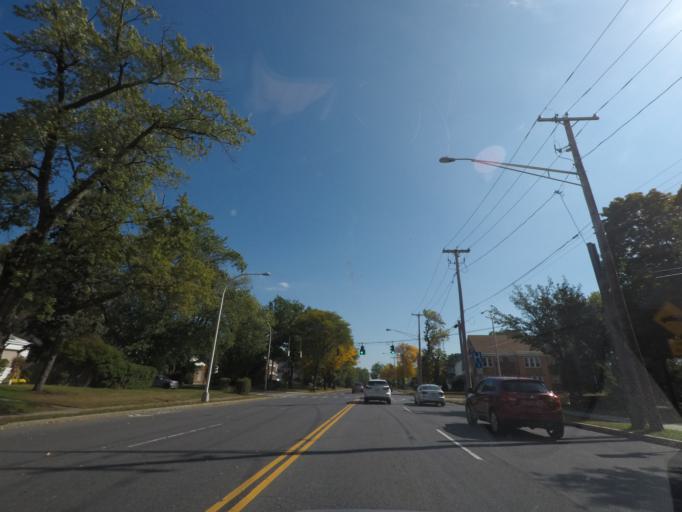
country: US
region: New York
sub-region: Albany County
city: Roessleville
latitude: 42.6782
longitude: -73.8004
